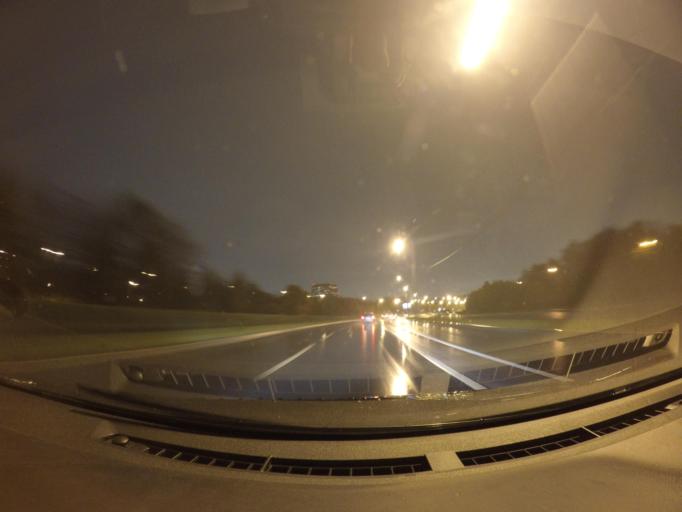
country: RU
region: Moscow
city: Tsaritsyno
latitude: 55.6533
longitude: 37.6547
